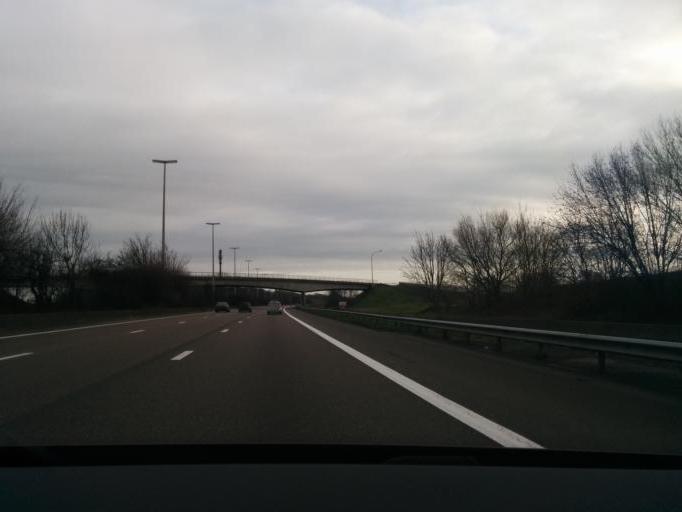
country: BE
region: Flanders
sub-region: Provincie Vlaams-Brabant
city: Boutersem
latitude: 50.8206
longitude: 4.8395
